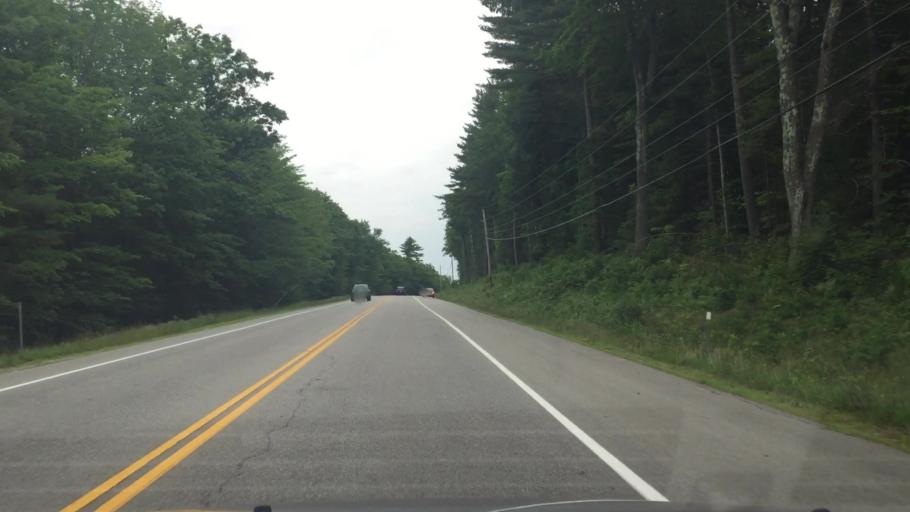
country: US
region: New Hampshire
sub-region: Carroll County
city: Moultonborough
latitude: 43.7823
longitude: -71.3794
